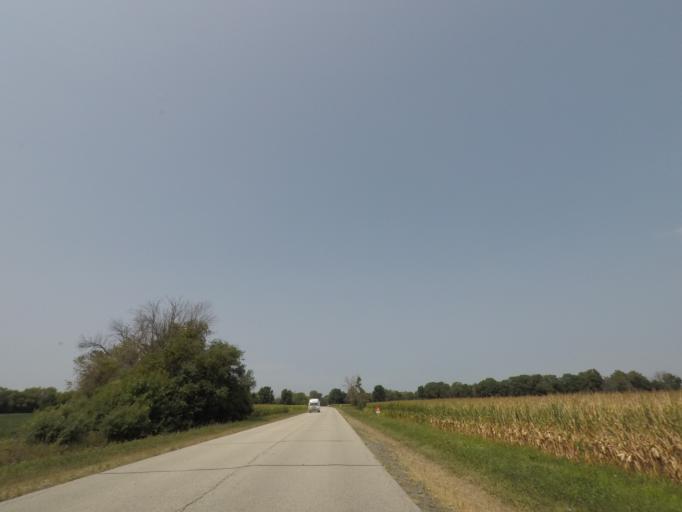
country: US
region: Wisconsin
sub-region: Waukesha County
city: Oconomowoc
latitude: 43.0664
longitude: -88.5464
